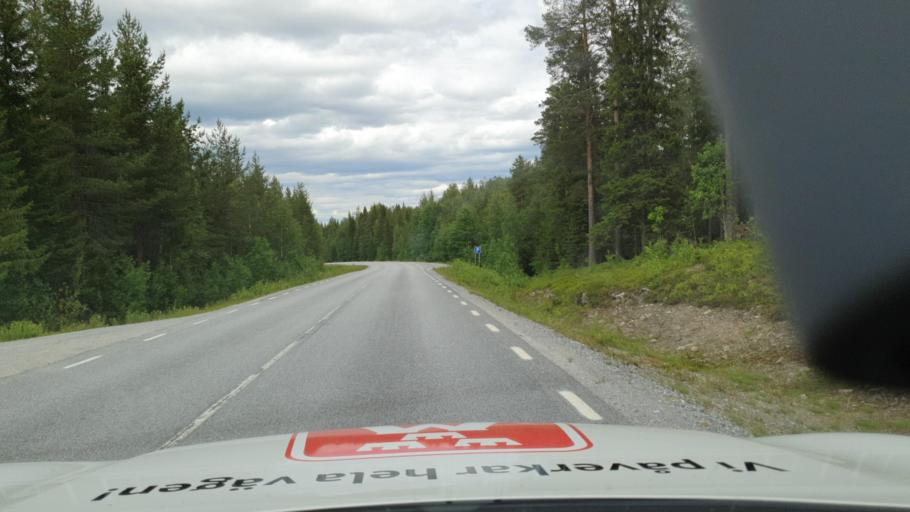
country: SE
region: Vaesterbotten
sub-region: Bjurholms Kommun
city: Bjurholm
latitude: 63.8975
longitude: 19.0695
